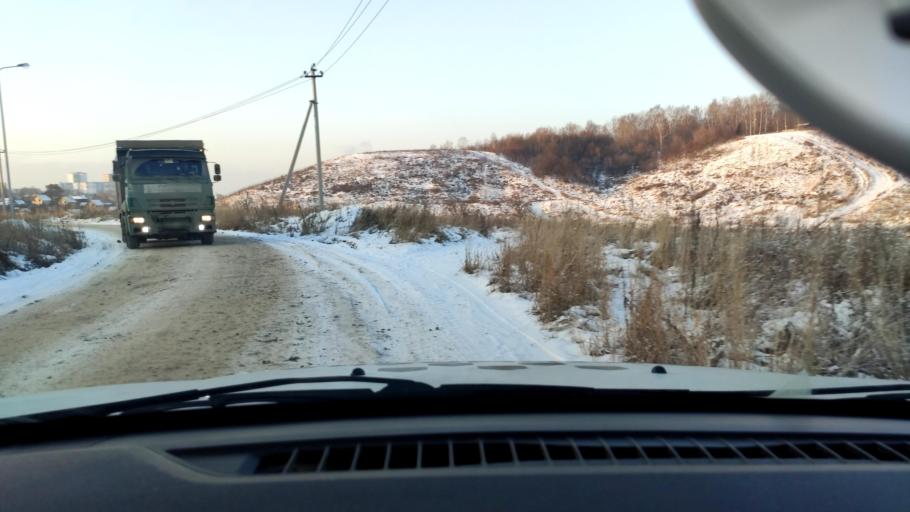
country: RU
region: Perm
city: Perm
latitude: 58.0283
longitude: 56.3499
